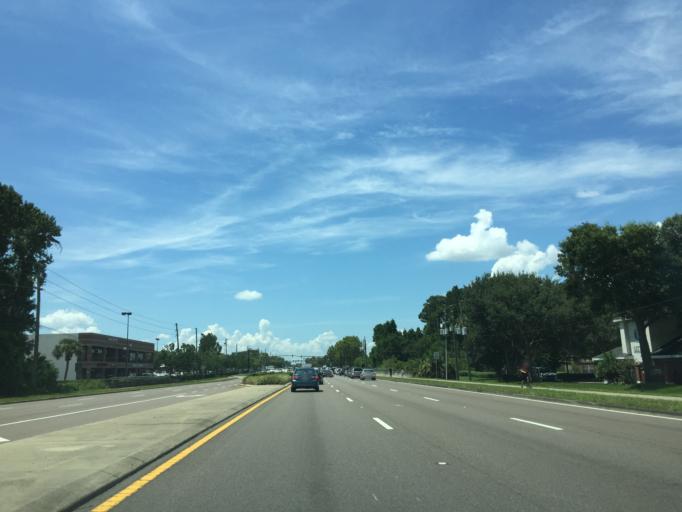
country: US
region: Florida
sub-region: Seminole County
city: Goldenrod
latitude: 28.6477
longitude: -81.2631
